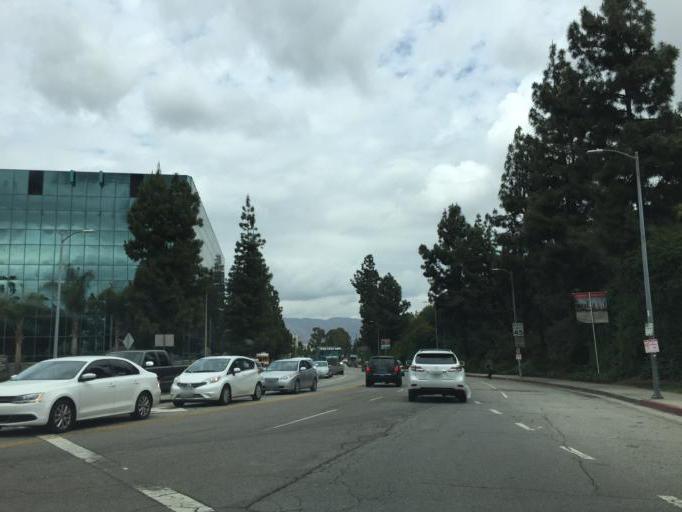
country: US
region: California
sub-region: Los Angeles County
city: Universal City
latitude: 34.1431
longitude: -118.3413
